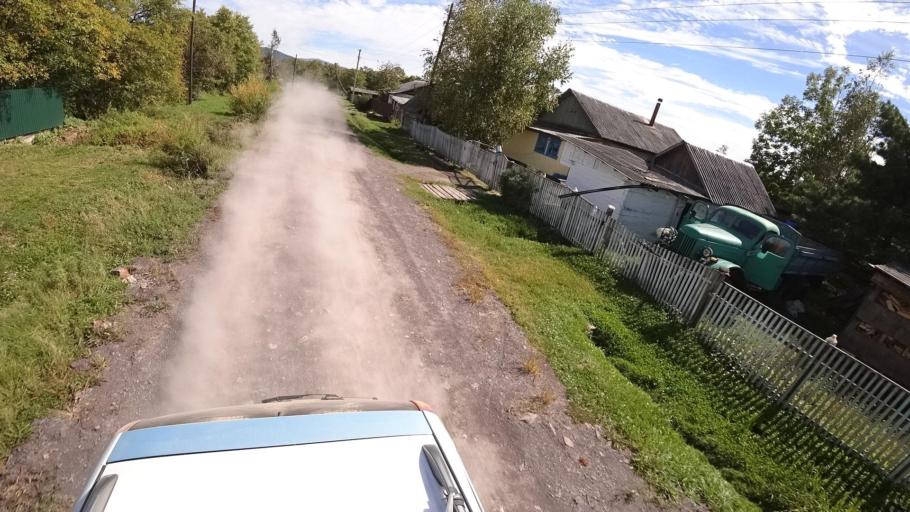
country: RU
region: Primorskiy
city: Yakovlevka
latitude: 44.4310
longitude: 133.5726
